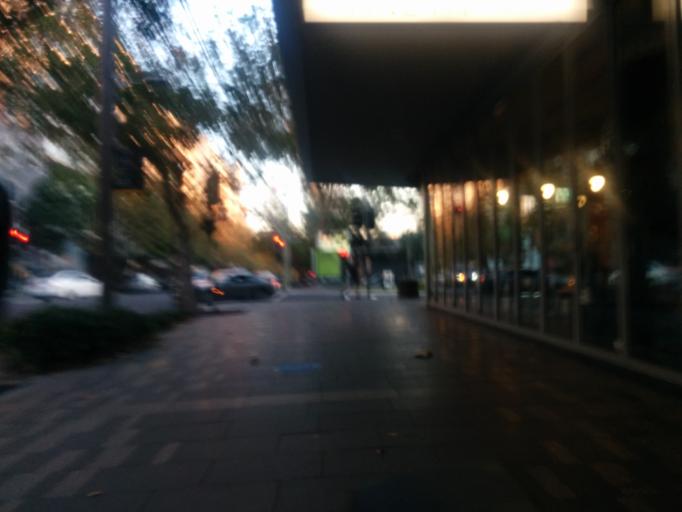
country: AU
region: New South Wales
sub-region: City of Sydney
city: Redfern
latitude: -33.8976
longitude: 151.2126
